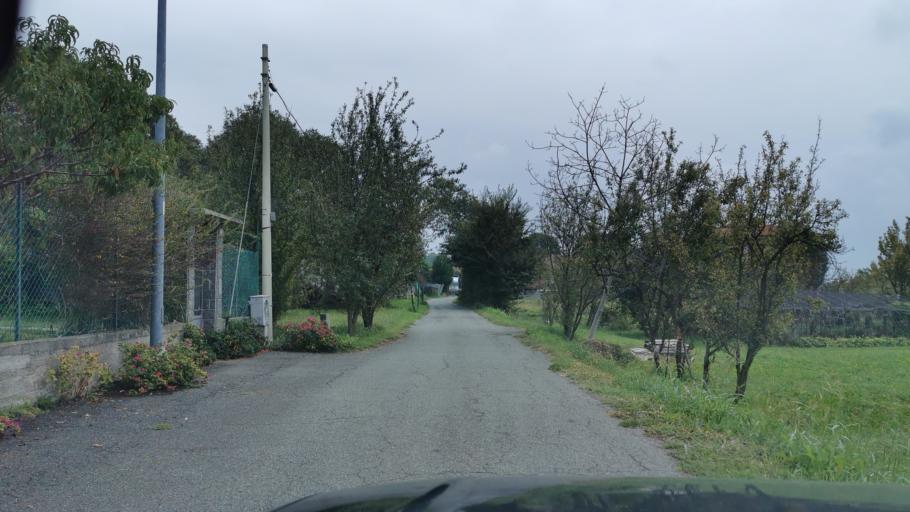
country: IT
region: Piedmont
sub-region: Provincia di Torino
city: Grosso
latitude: 45.2574
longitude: 7.5720
